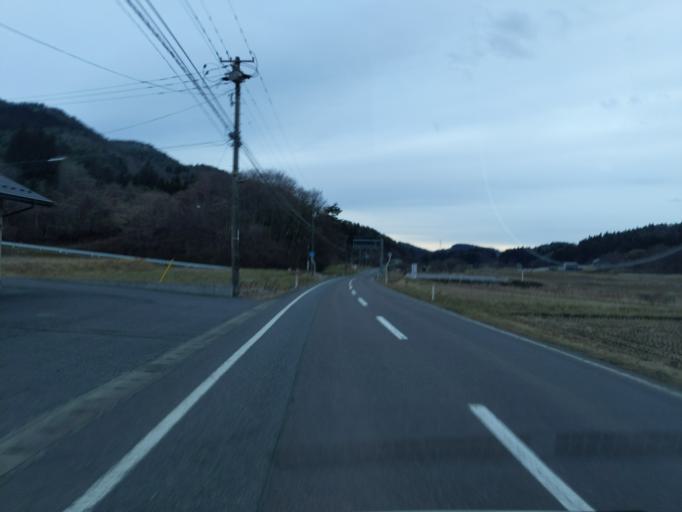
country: JP
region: Iwate
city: Mizusawa
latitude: 39.0585
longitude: 141.2879
